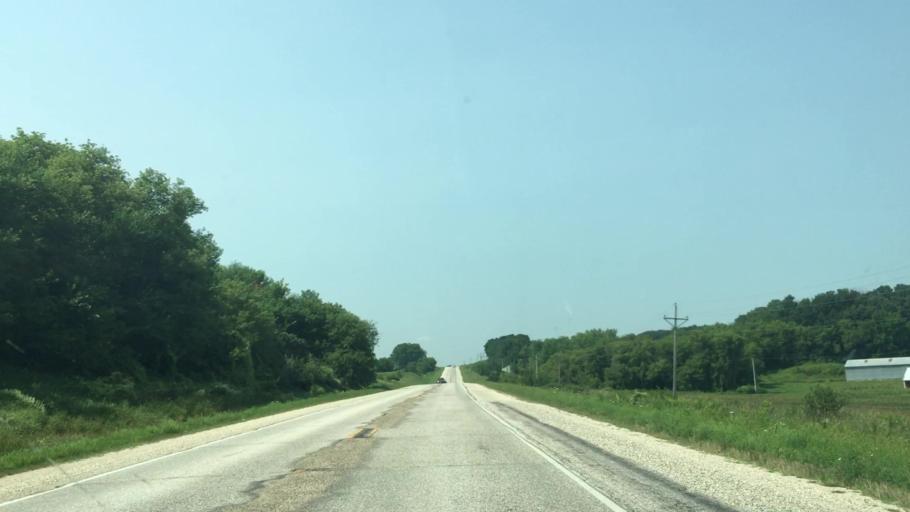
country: US
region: Iowa
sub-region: Fayette County
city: West Union
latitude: 43.0827
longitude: -91.8452
